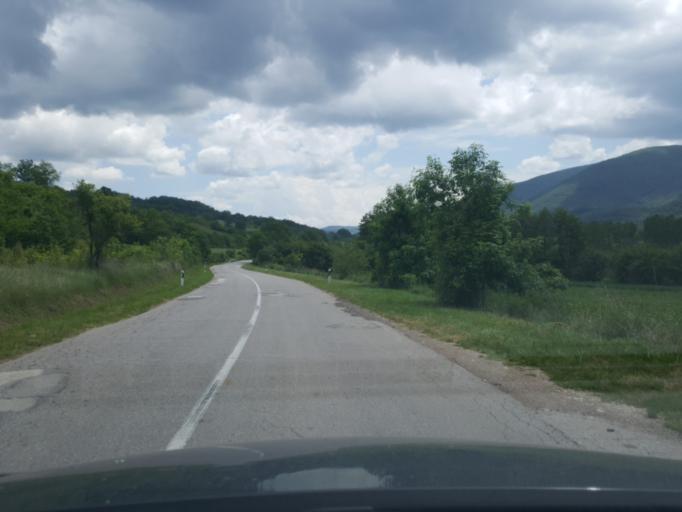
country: RS
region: Central Serbia
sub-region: Zajecarski Okrug
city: Soko Banja
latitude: 43.6423
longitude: 21.9464
